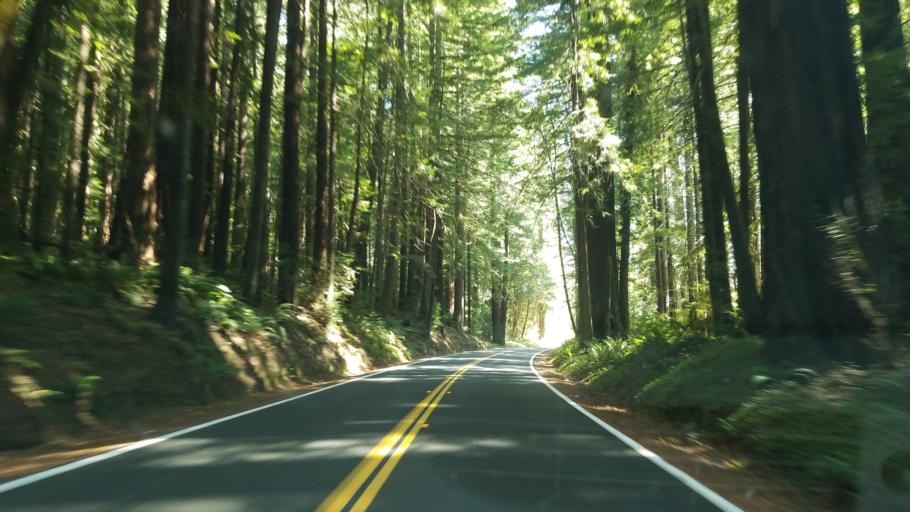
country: US
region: California
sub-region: Humboldt County
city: Redway
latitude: 40.3335
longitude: -123.9309
